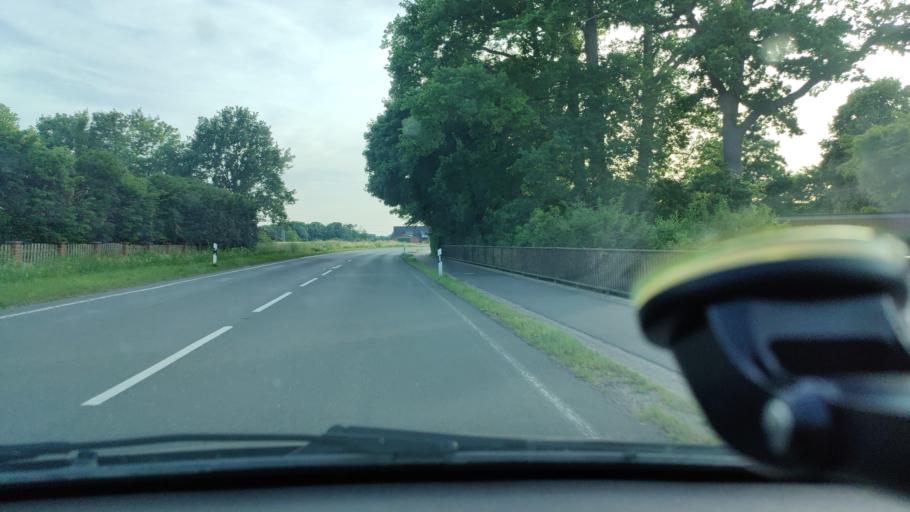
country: DE
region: North Rhine-Westphalia
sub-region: Regierungsbezirk Munster
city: Legden
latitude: 52.0104
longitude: 7.1587
